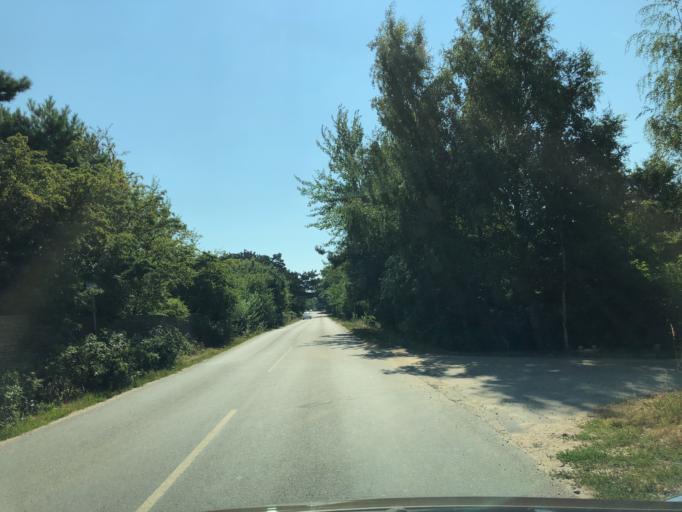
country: DK
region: Zealand
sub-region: Odsherred Kommune
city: Asnaes
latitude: 55.9835
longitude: 11.3060
